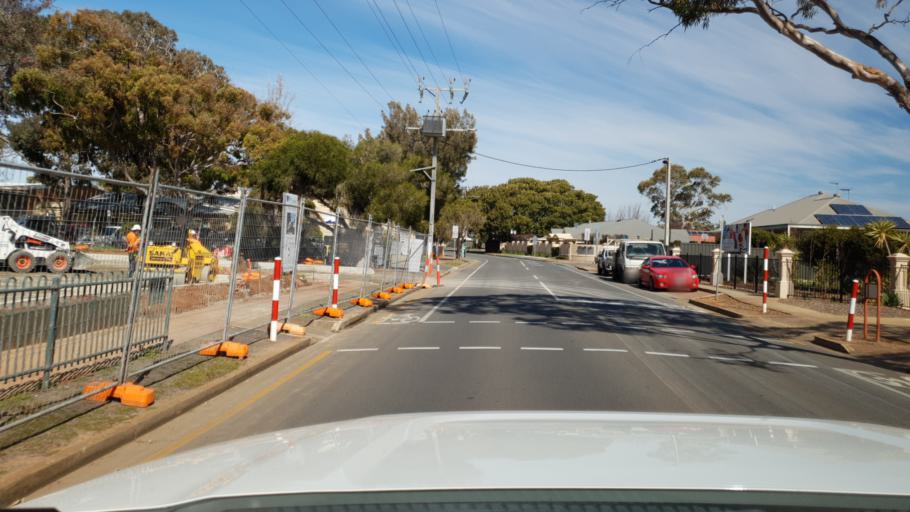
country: AU
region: South Australia
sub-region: Adelaide
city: Brighton
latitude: -35.0118
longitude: 138.5188
